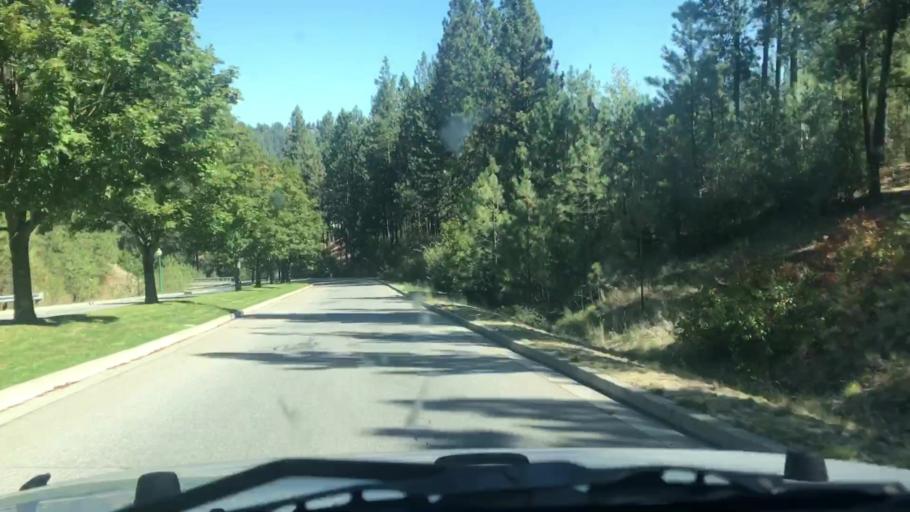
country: US
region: Washington
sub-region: Spokane County
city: Spokane
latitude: 47.5949
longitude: -117.4176
